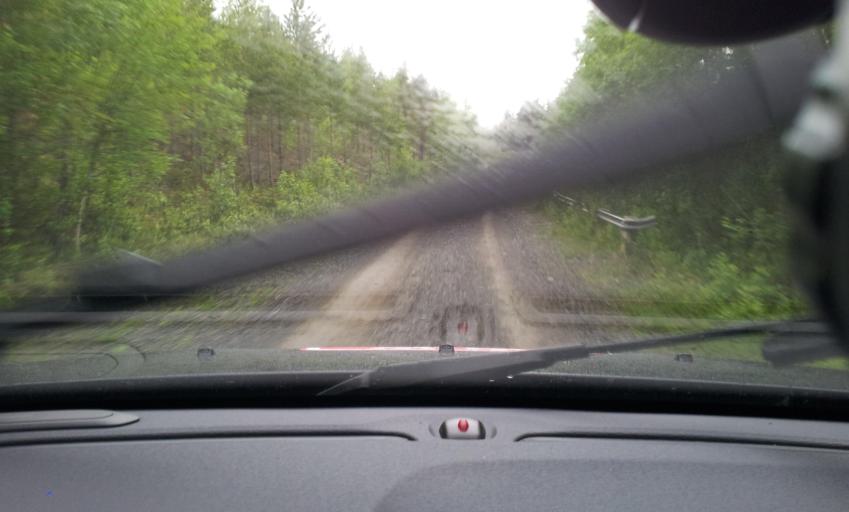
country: SE
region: Jaemtland
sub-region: Are Kommun
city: Jarpen
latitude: 63.1920
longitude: 13.4230
